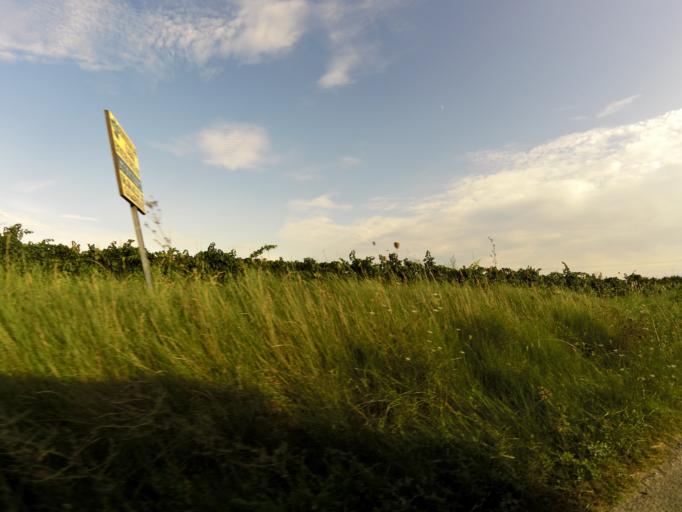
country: FR
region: Languedoc-Roussillon
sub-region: Departement du Gard
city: Gallargues-le-Montueux
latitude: 43.7094
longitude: 4.1698
